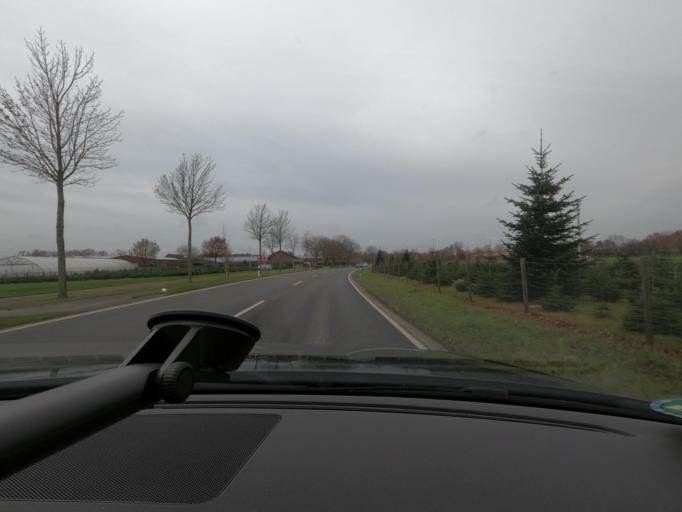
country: DE
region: North Rhine-Westphalia
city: Tonisvorst
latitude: 51.3482
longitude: 6.4707
